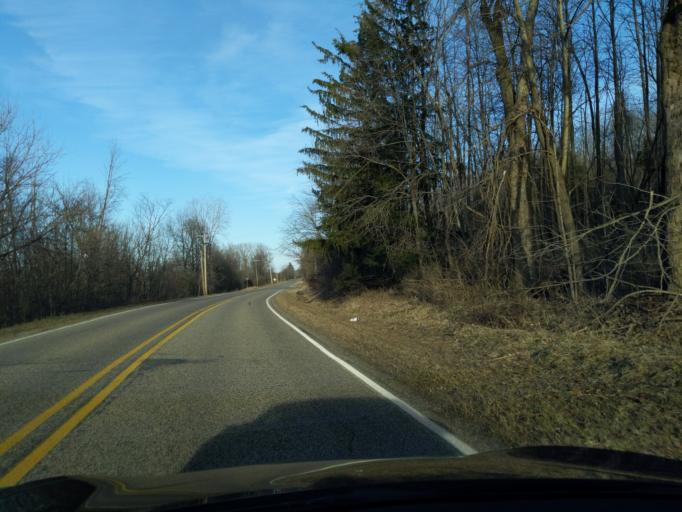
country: US
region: Michigan
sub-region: Ionia County
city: Ionia
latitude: 42.9630
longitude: -85.0945
